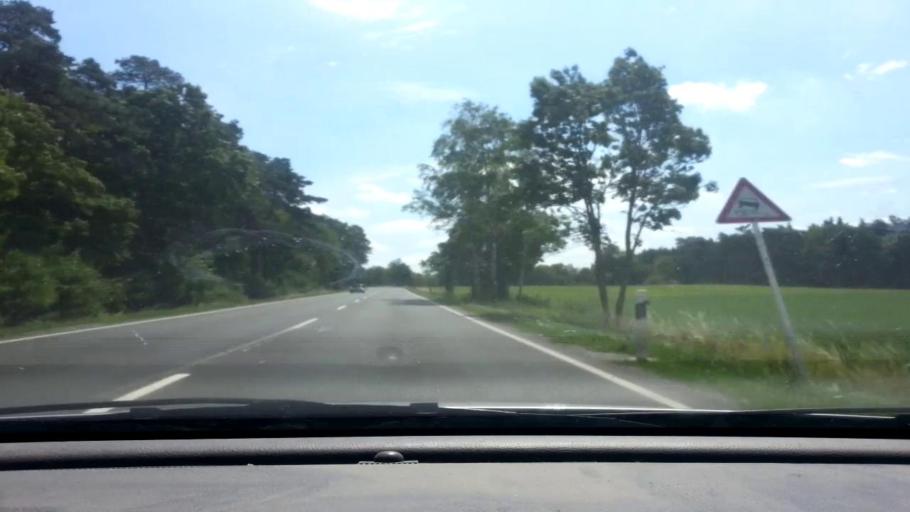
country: DE
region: Bavaria
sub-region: Upper Franconia
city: Emtmannsberg
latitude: 49.9058
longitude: 11.6806
